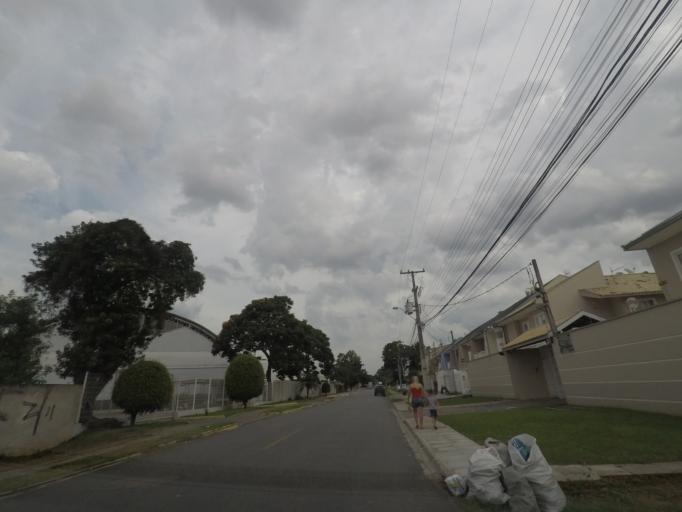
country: BR
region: Parana
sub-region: Sao Jose Dos Pinhais
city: Sao Jose dos Pinhais
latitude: -25.4879
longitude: -49.2460
